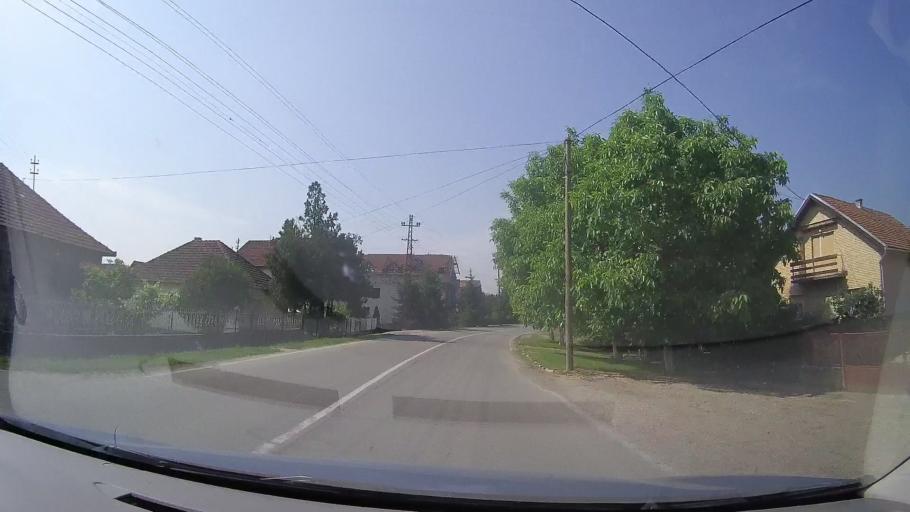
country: RS
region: Autonomna Pokrajina Vojvodina
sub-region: Srednjebanatski Okrug
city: Secanj
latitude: 45.3679
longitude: 20.7769
